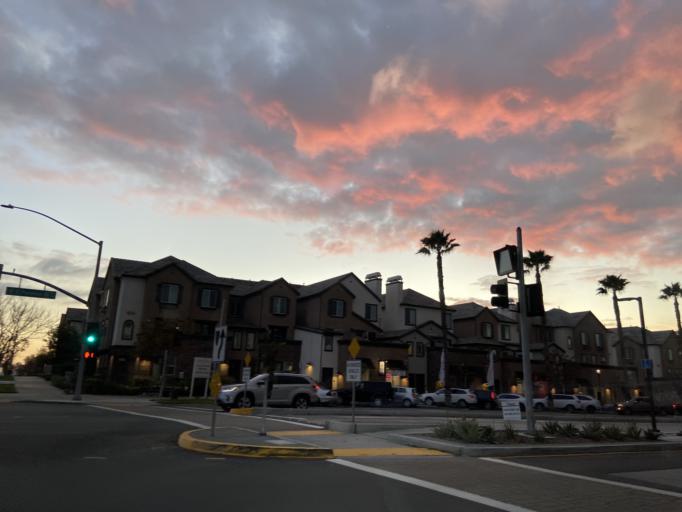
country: US
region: California
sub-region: San Diego County
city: Bonita
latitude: 32.6268
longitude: -116.9748
